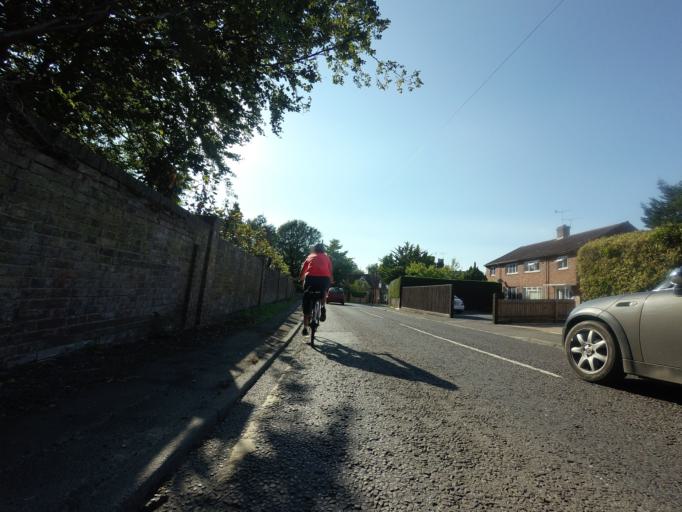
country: GB
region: England
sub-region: Kent
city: Tenterden
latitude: 51.0652
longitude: 0.6822
